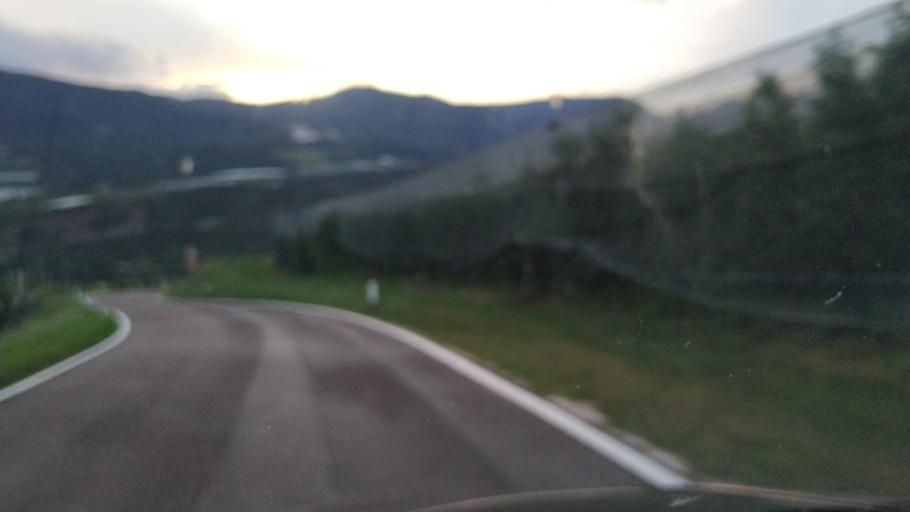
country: IT
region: Trentino-Alto Adige
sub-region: Provincia di Trento
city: Fondo
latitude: 46.4372
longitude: 11.1248
